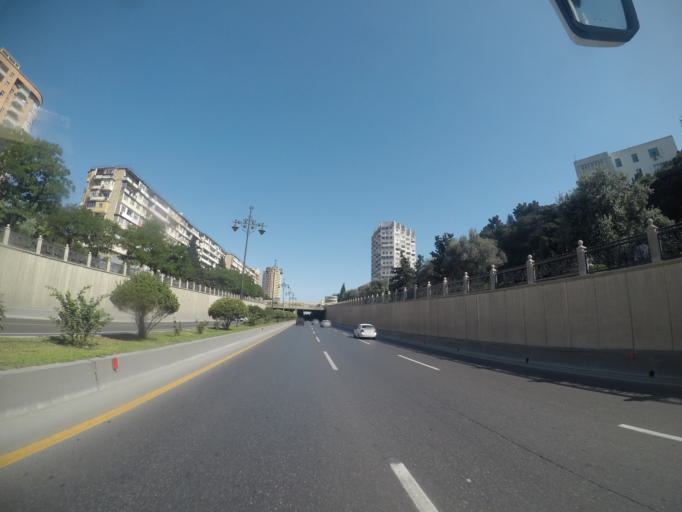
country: AZ
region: Baki
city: Bilajari
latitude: 40.4085
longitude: 49.8051
